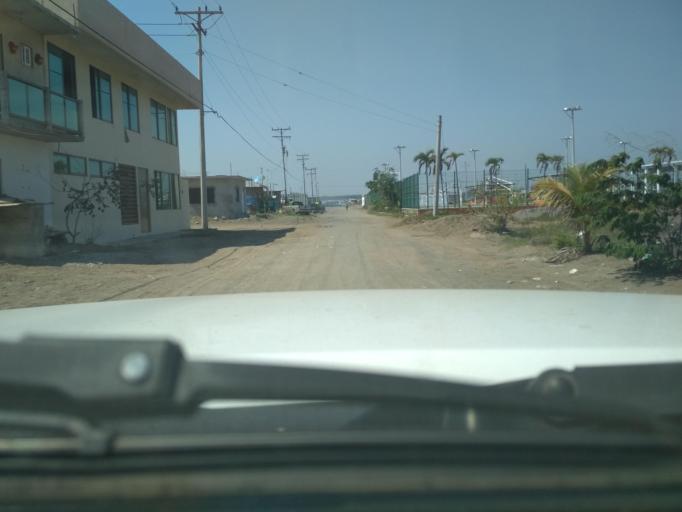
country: MX
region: Veracruz
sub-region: Veracruz
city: Lomas de Rio Medio Cuatro
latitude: 19.1916
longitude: -96.1974
